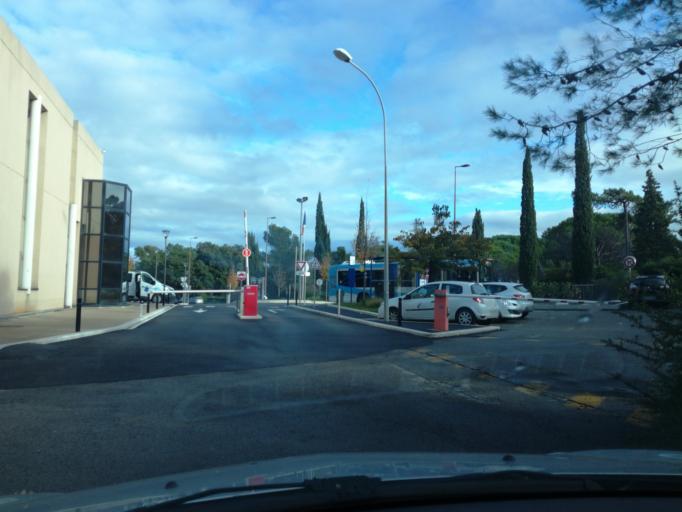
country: FR
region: Provence-Alpes-Cote d'Azur
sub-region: Departement des Alpes-Maritimes
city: Pegomas
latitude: 43.6195
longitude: 6.9302
